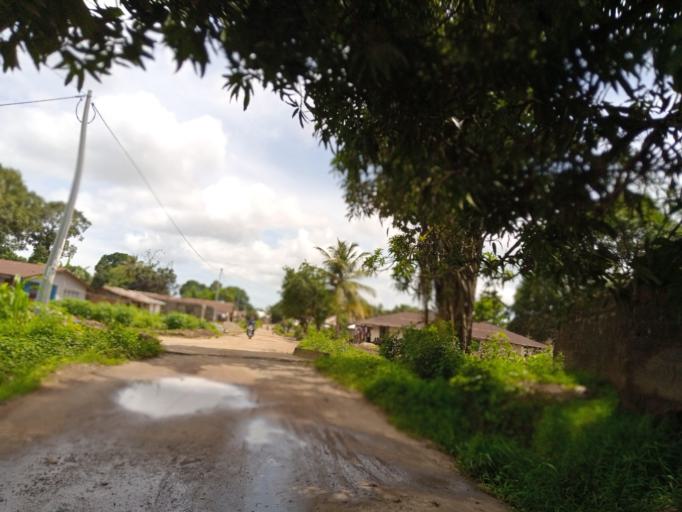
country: SL
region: Northern Province
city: Masoyila
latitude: 8.6077
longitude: -13.1881
